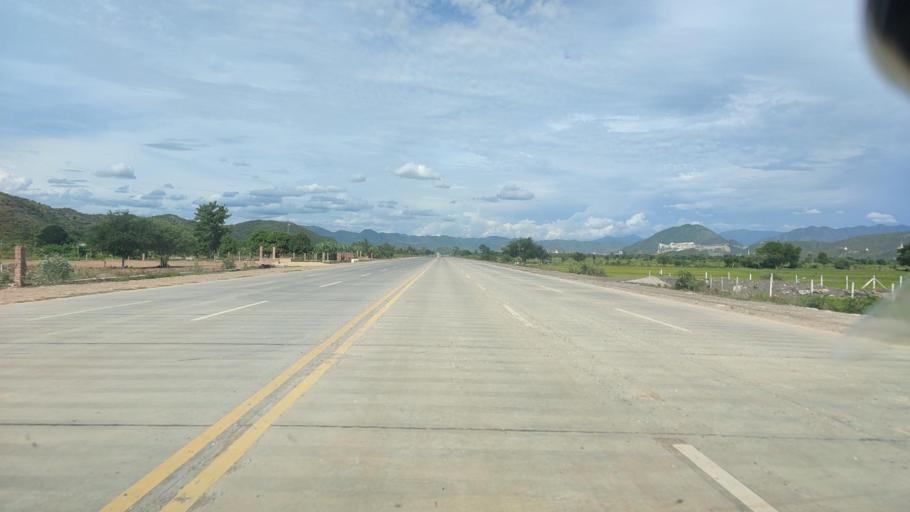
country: MM
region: Mandalay
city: Kyaukse
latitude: 21.5948
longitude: 96.1594
